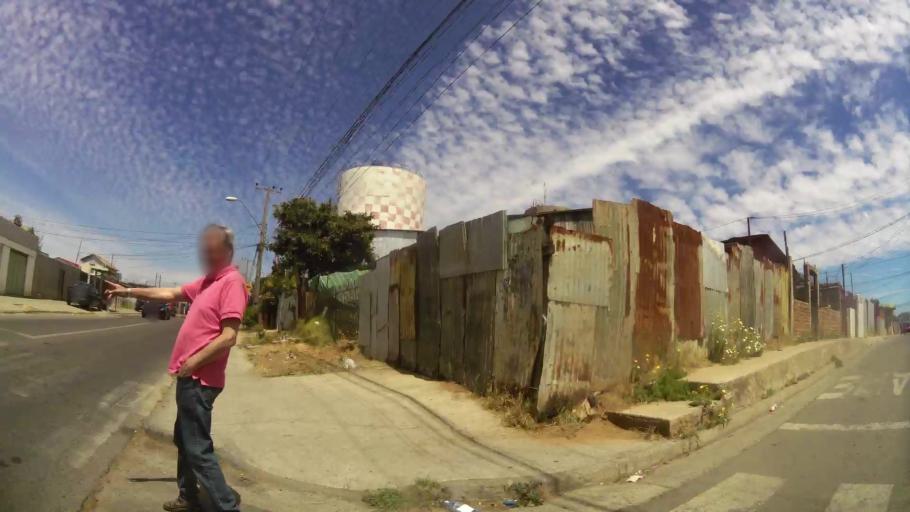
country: CL
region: Valparaiso
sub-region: Provincia de Valparaiso
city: Vina del Mar
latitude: -33.0645
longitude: -71.5714
